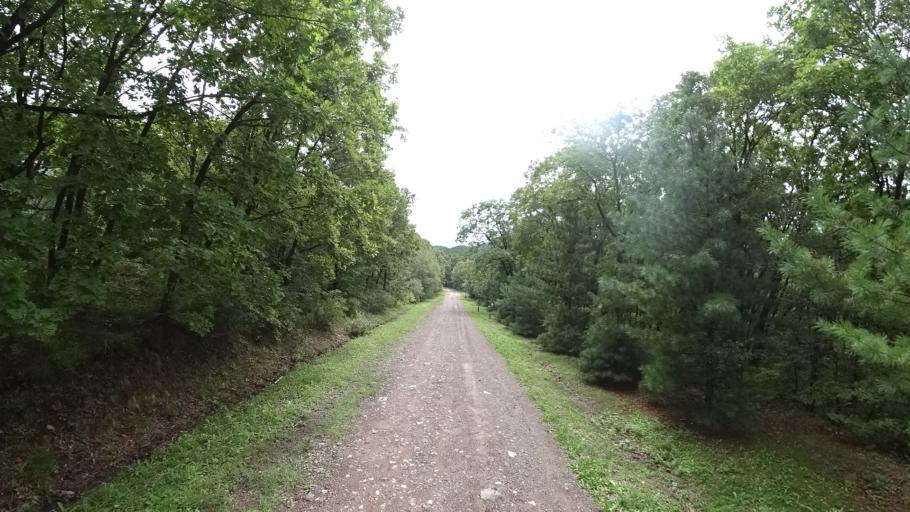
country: RU
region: Primorskiy
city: Monastyrishche
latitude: 44.1690
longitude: 132.5385
